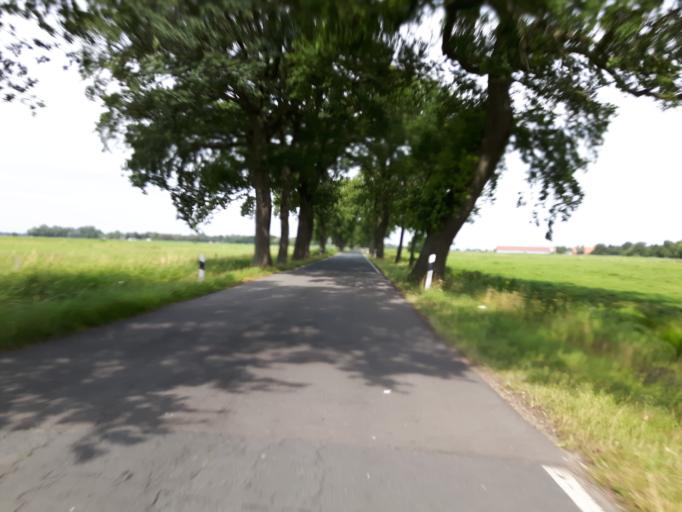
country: DE
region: Lower Saxony
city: Rastede
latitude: 53.3335
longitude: 8.2553
